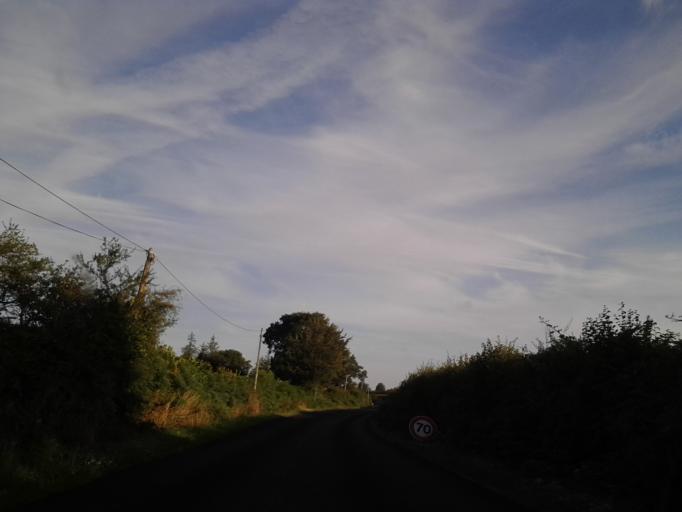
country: FR
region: Lower Normandy
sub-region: Departement de la Manche
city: Digosville
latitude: 49.5903
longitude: -1.4709
